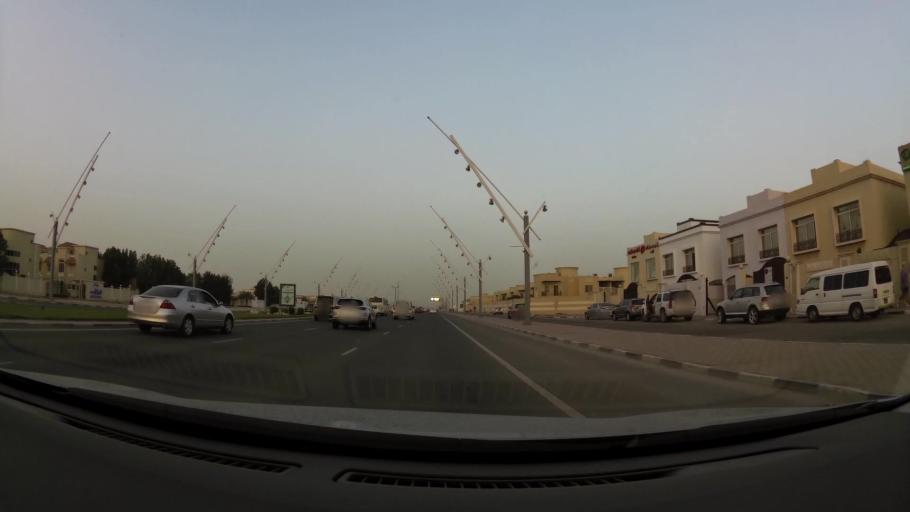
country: QA
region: Baladiyat ar Rayyan
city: Ar Rayyan
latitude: 25.2621
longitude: 51.4574
